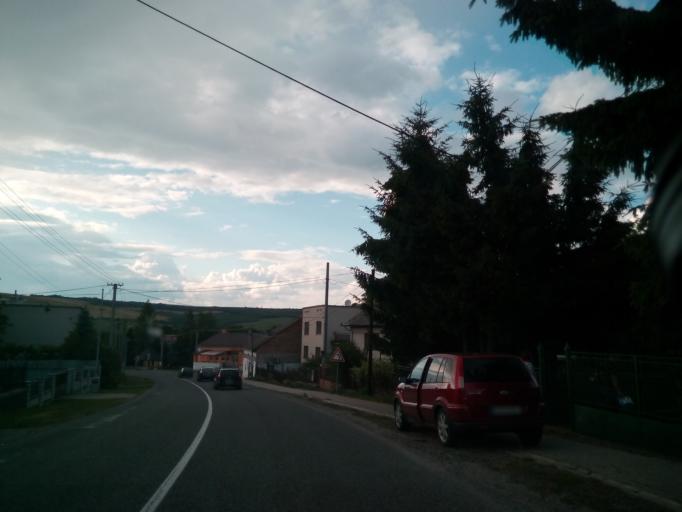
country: SK
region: Kosicky
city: Kosice
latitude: 48.6559
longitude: 21.4017
